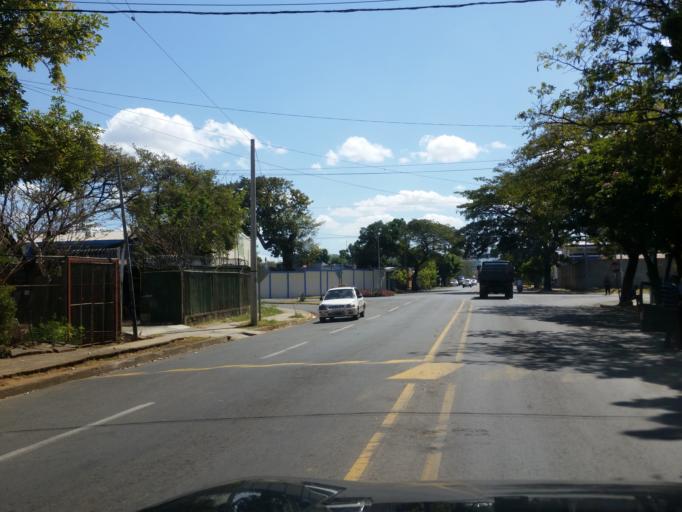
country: NI
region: Managua
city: Managua
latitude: 12.1575
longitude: -86.2765
